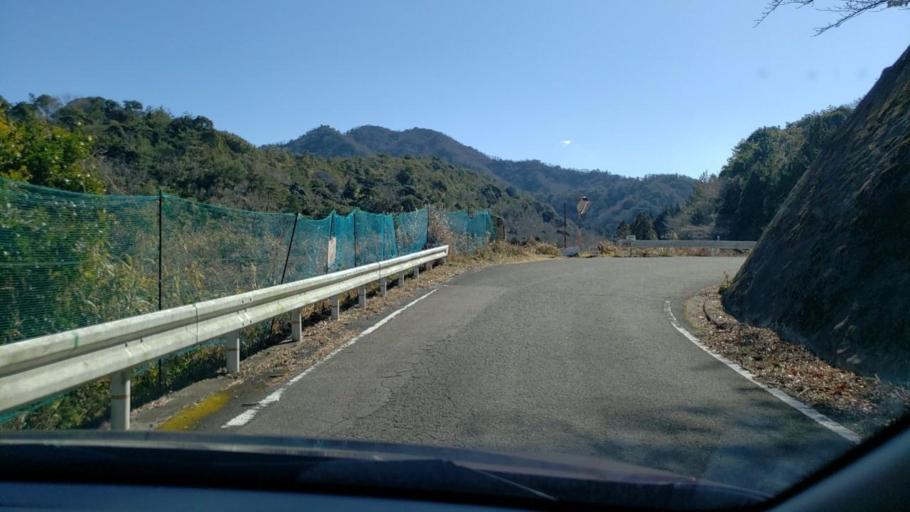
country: JP
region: Tokushima
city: Narutocho-mitsuishi
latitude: 34.2040
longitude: 134.5531
